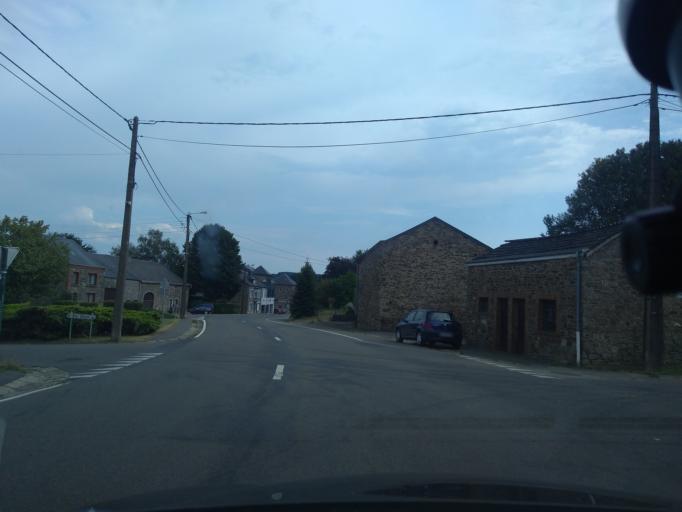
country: BE
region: Wallonia
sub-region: Province du Luxembourg
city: Libin
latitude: 49.9855
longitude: 5.2530
